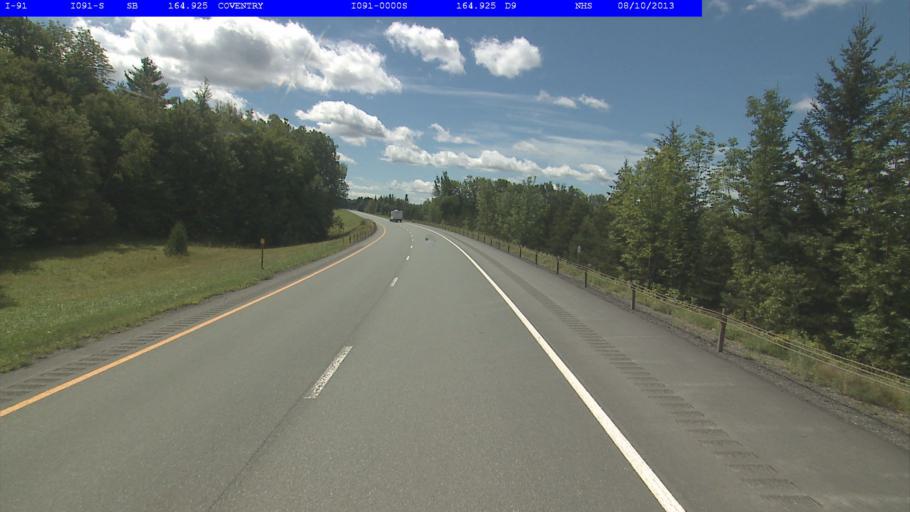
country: US
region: Vermont
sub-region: Orleans County
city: Newport
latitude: 44.8540
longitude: -72.1942
